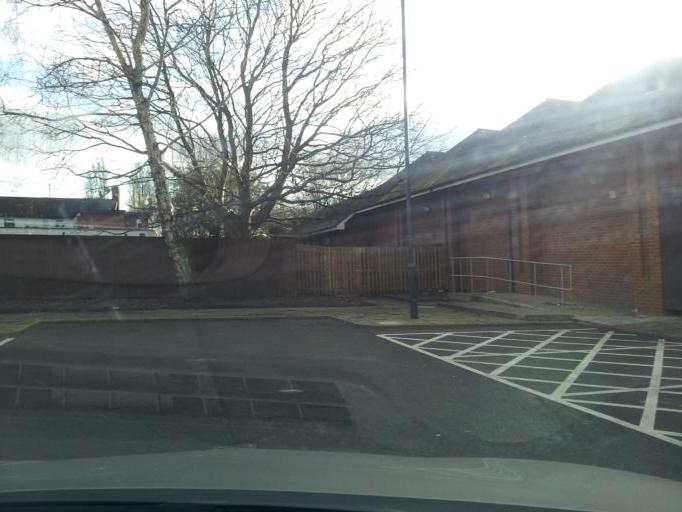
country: GB
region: England
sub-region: Nottinghamshire
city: Kimberley
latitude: 52.9561
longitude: -1.2286
